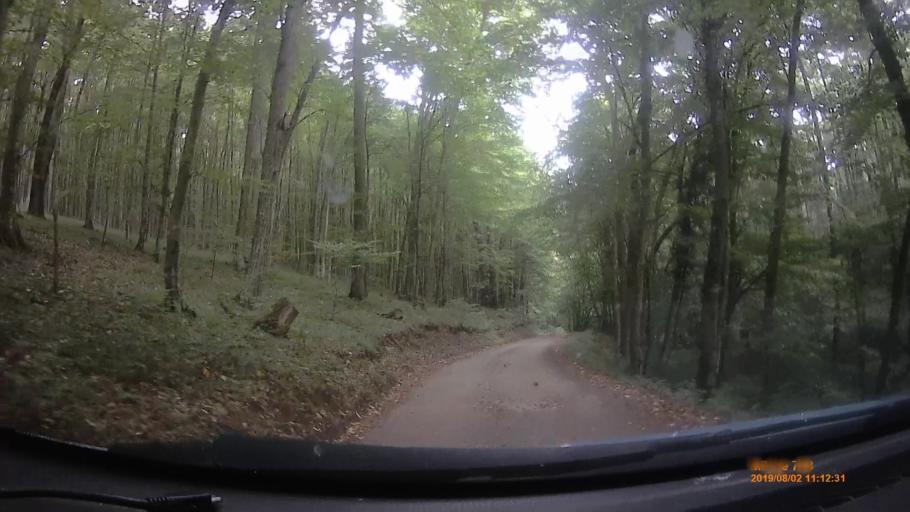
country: HU
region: Baranya
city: Buekkoesd
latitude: 46.1097
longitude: 17.9352
